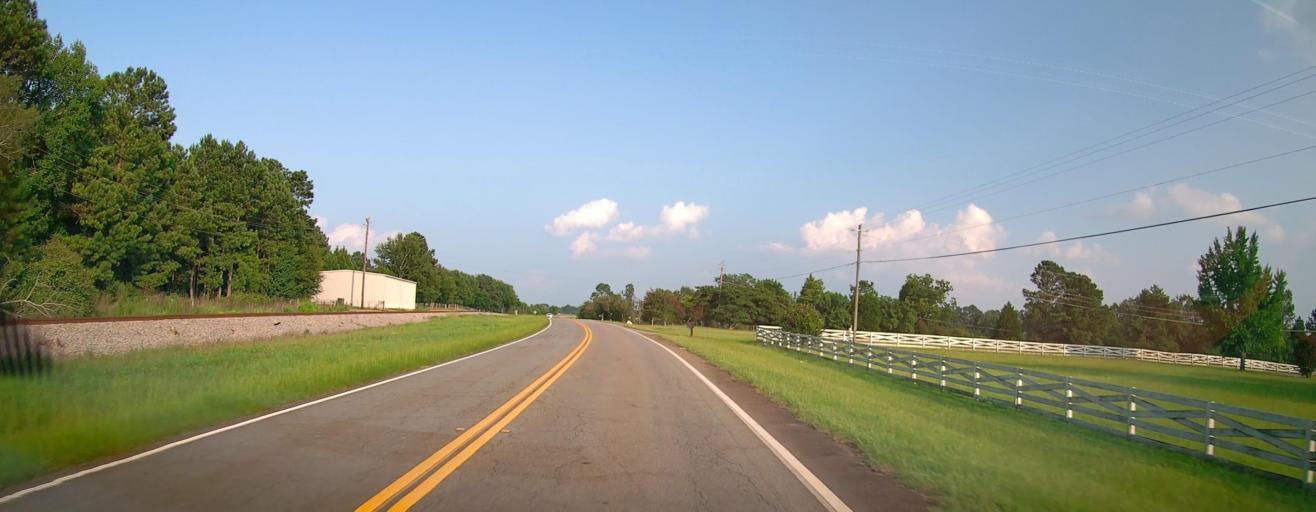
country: US
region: Georgia
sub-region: Jones County
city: Gray
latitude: 33.0425
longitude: -83.5507
